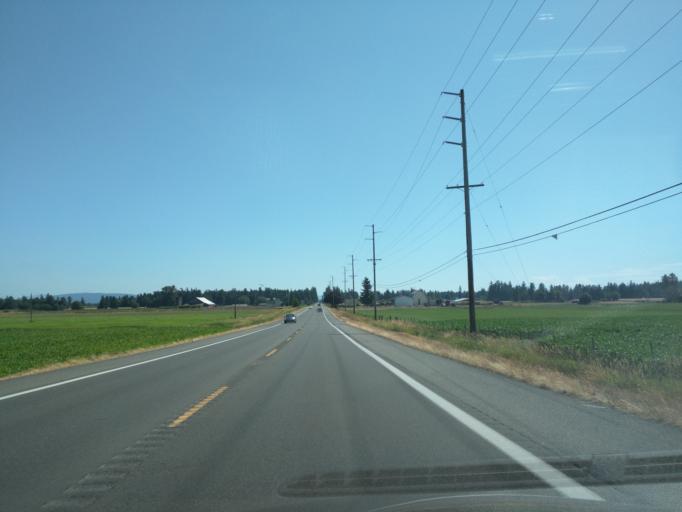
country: US
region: Washington
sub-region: Whatcom County
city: Lynden
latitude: 48.9075
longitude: -122.4422
